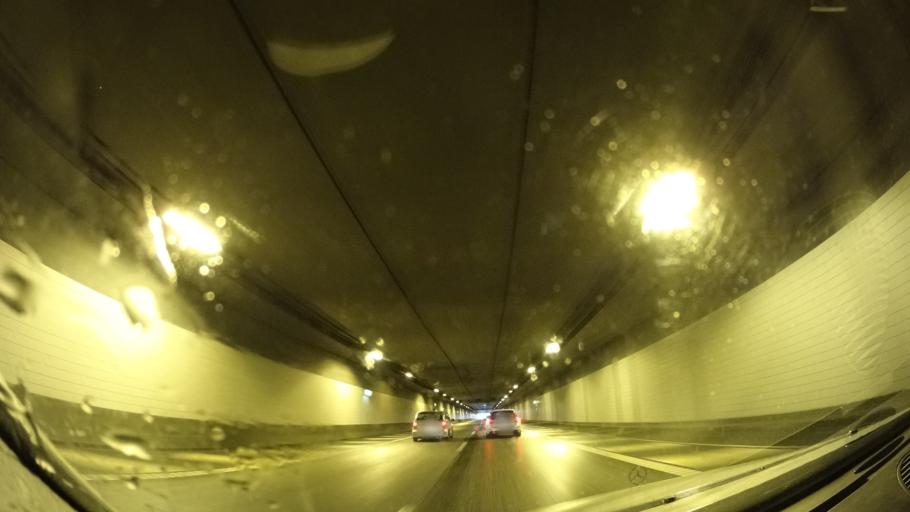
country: DK
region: Capital Region
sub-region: Tarnby Kommune
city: Tarnby
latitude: 55.6294
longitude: 12.6024
